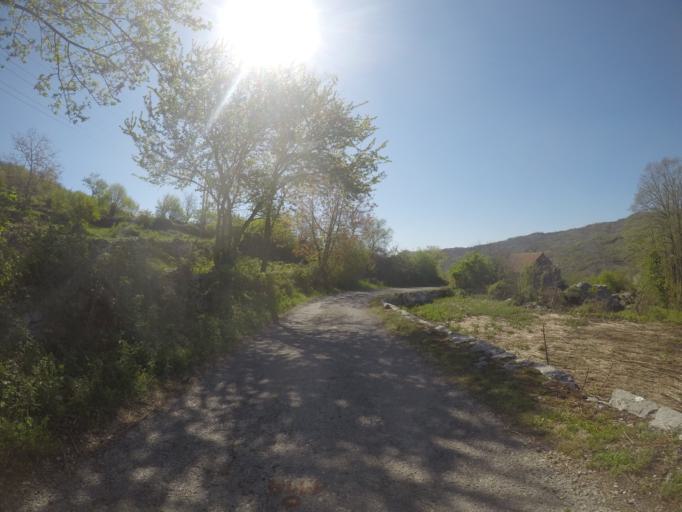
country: ME
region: Danilovgrad
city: Danilovgrad
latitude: 42.5215
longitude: 19.0504
